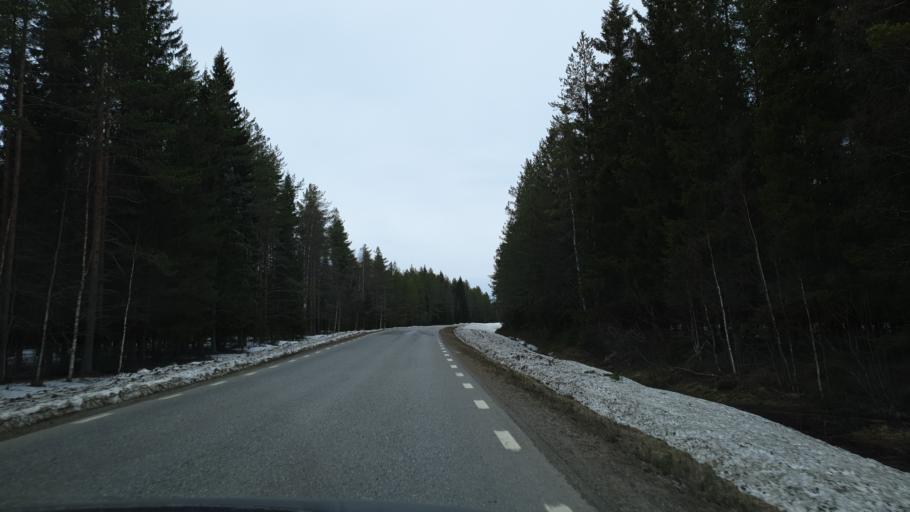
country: SE
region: Vaesterbotten
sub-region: Robertsfors Kommun
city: Robertsfors
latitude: 64.4014
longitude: 20.8817
